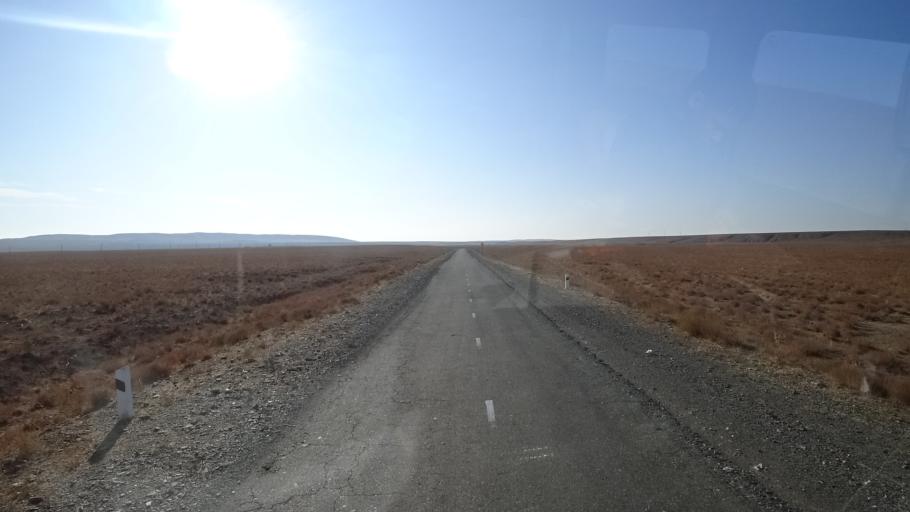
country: UZ
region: Navoiy
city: Karmana Shahri
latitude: 40.2623
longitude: 65.4995
